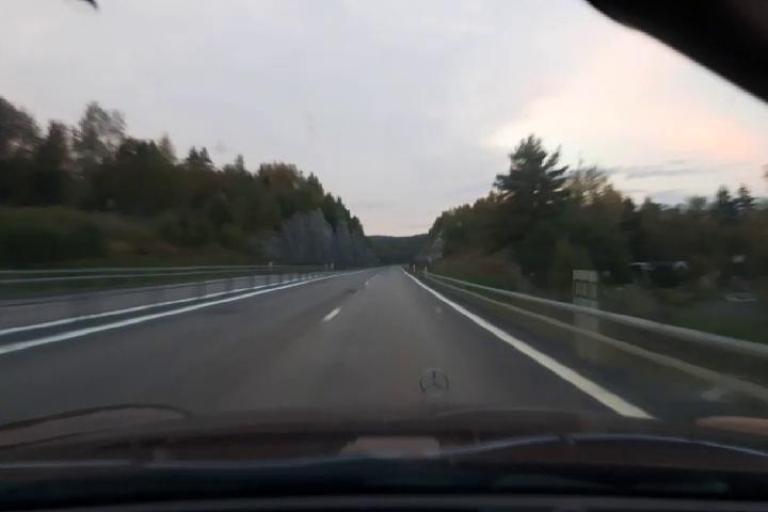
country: SE
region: Vaesternorrland
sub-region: Haernoesands Kommun
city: Haernoesand
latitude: 62.8332
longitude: 17.9677
